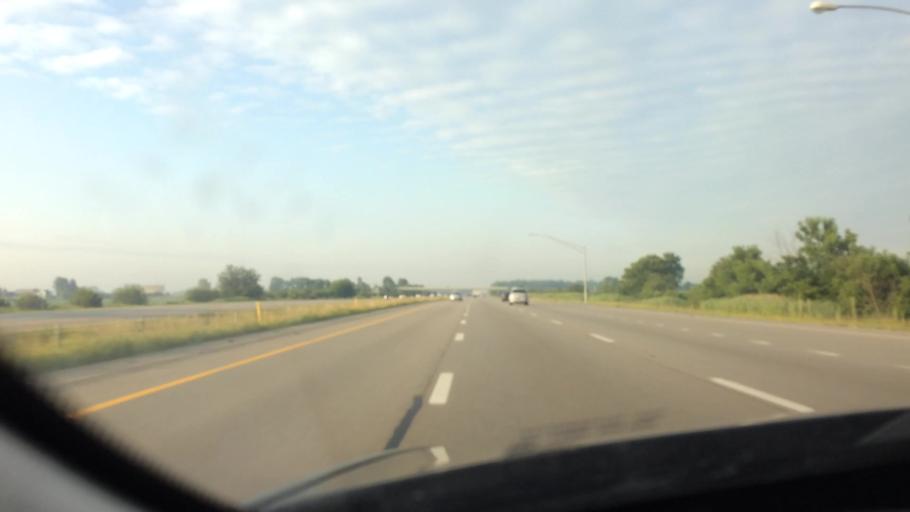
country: US
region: Ohio
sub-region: Wood County
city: Bowling Green
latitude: 41.3316
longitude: -83.6261
